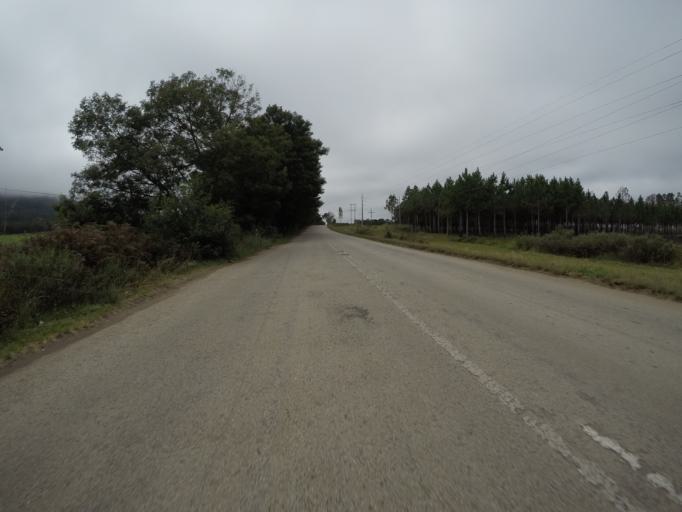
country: ZA
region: Eastern Cape
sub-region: Cacadu District Municipality
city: Kareedouw
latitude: -33.9966
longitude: 24.1445
